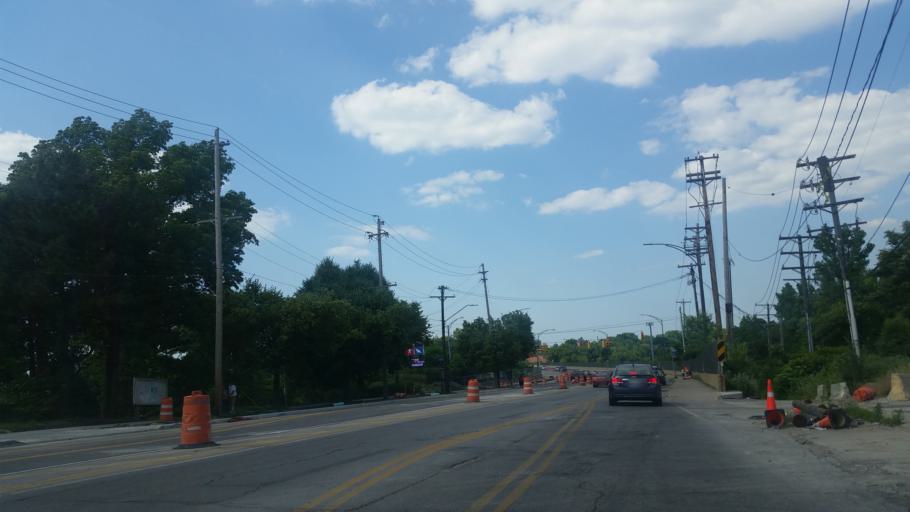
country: US
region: Ohio
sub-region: Cuyahoga County
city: Brooklyn Heights
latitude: 41.4433
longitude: -81.7037
